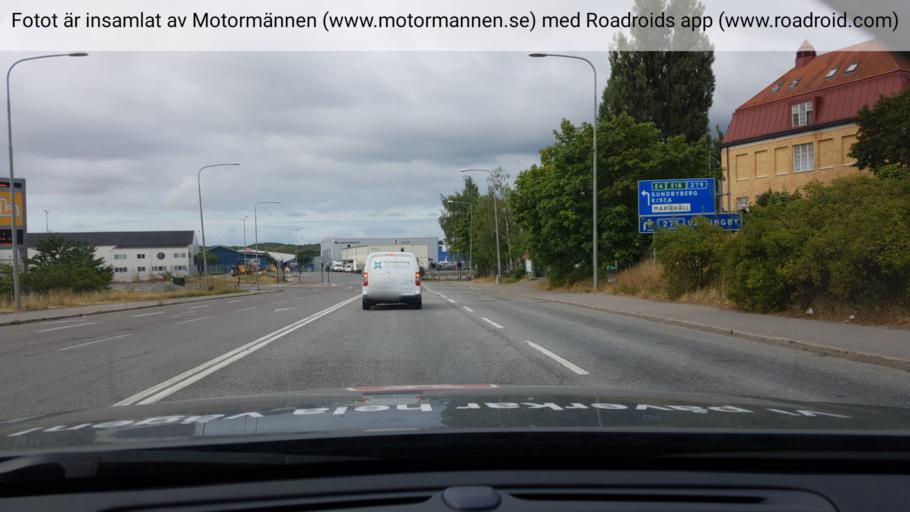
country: SE
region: Stockholm
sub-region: Stockholms Kommun
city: Bromma
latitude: 59.3630
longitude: 17.9407
